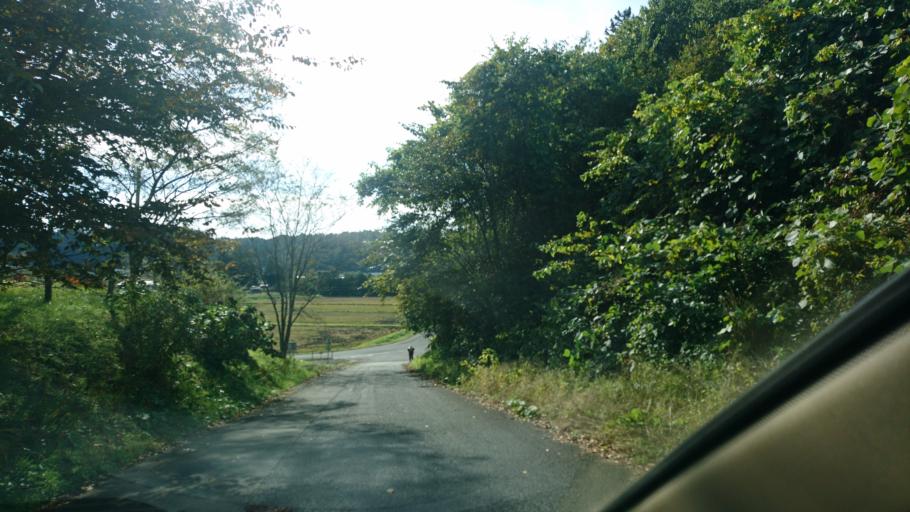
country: JP
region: Iwate
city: Ichinoseki
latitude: 39.0203
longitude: 141.3445
